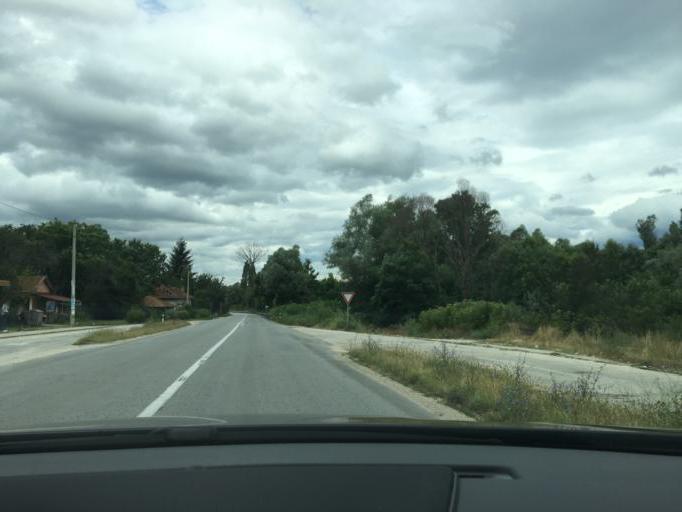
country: MK
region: Opstina Rankovce
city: Rankovce
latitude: 42.1723
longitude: 22.2067
